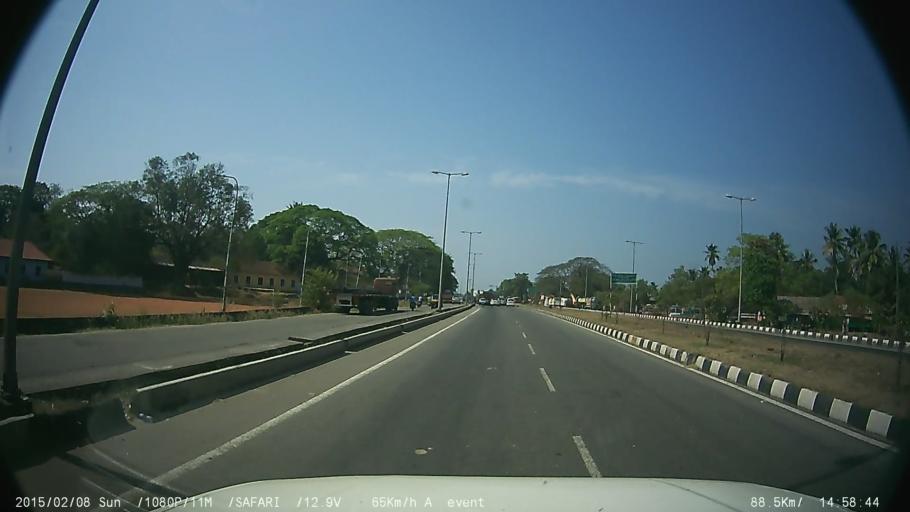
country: IN
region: Kerala
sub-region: Thrissur District
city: Kizhake Chalakudi
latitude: 10.3050
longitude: 76.3352
